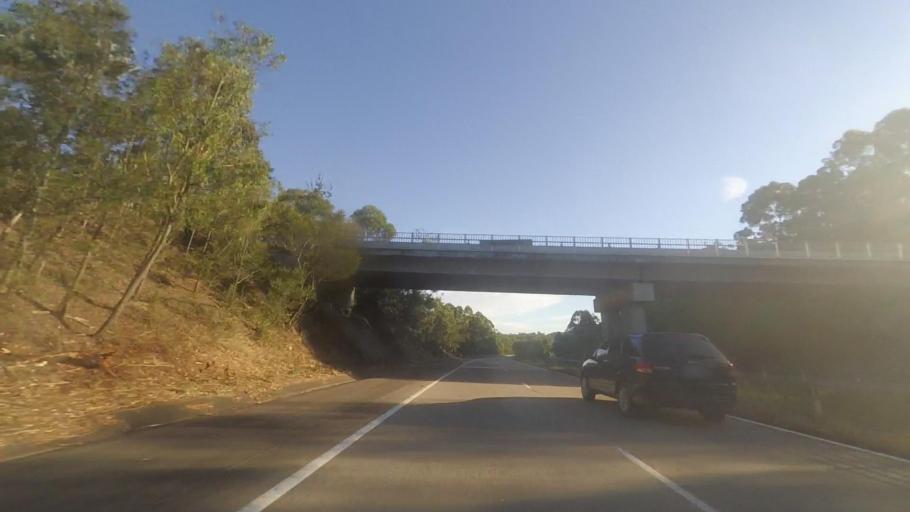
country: AU
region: New South Wales
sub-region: Great Lakes
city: Bulahdelah
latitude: -32.3011
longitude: 152.3462
